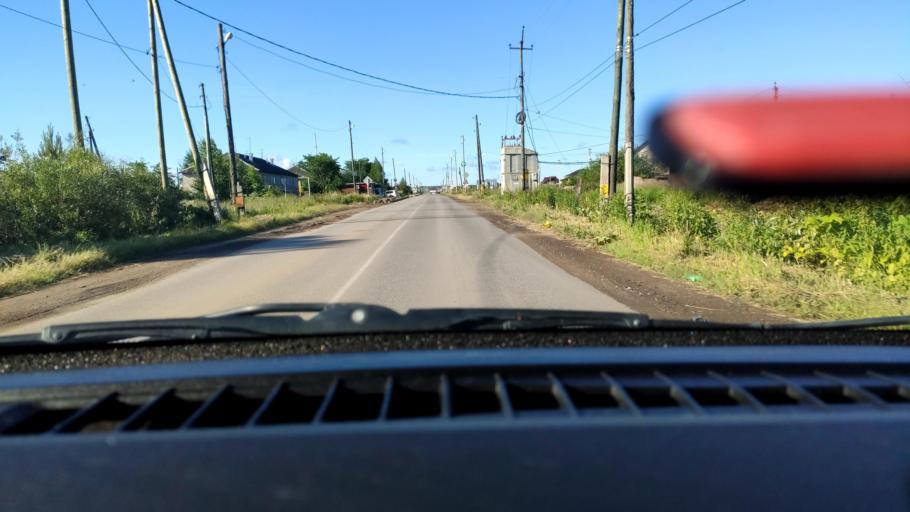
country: RU
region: Perm
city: Kultayevo
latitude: 57.8736
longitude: 55.9190
